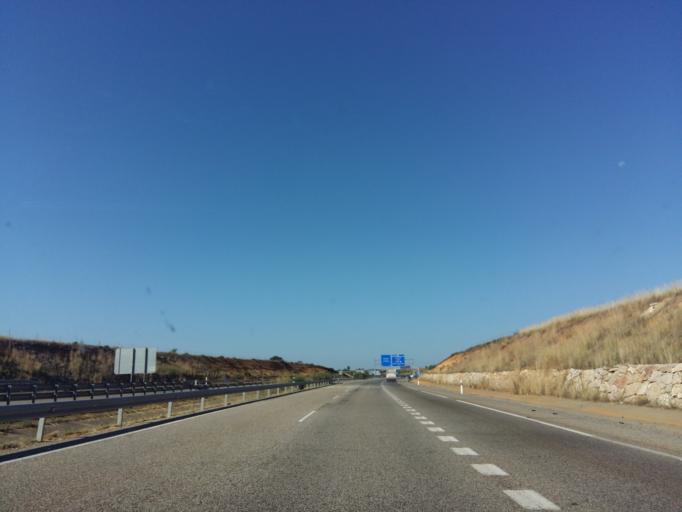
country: ES
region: Castille and Leon
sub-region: Provincia de Leon
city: San Andres del Rabanedo
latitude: 42.5739
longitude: -5.6322
